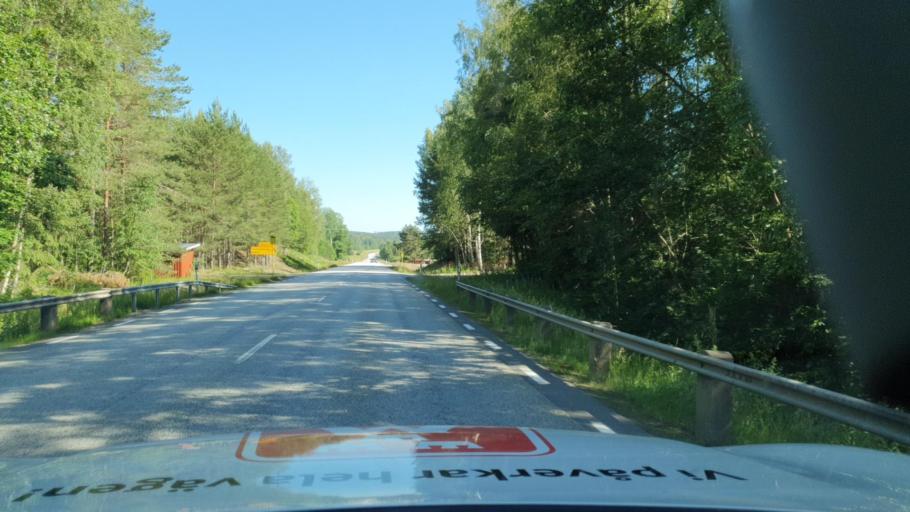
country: SE
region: Vaermland
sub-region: Storfors Kommun
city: Storfors
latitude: 59.5070
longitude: 14.3098
